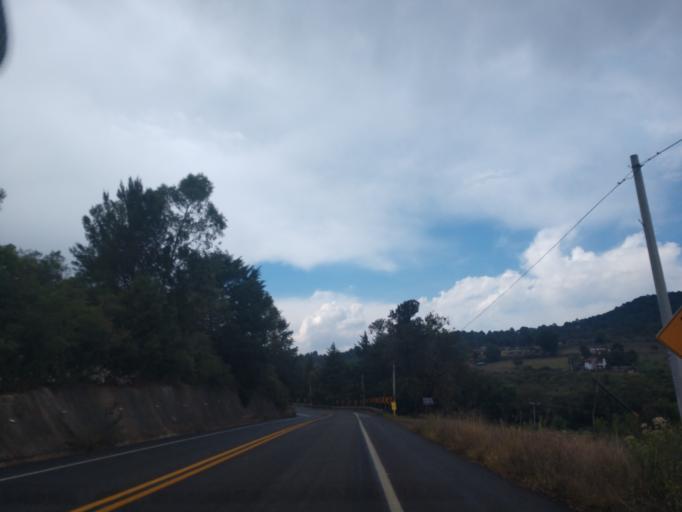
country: MX
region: Jalisco
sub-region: Mazamitla
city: Mazamitla
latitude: 19.9409
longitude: -103.0604
